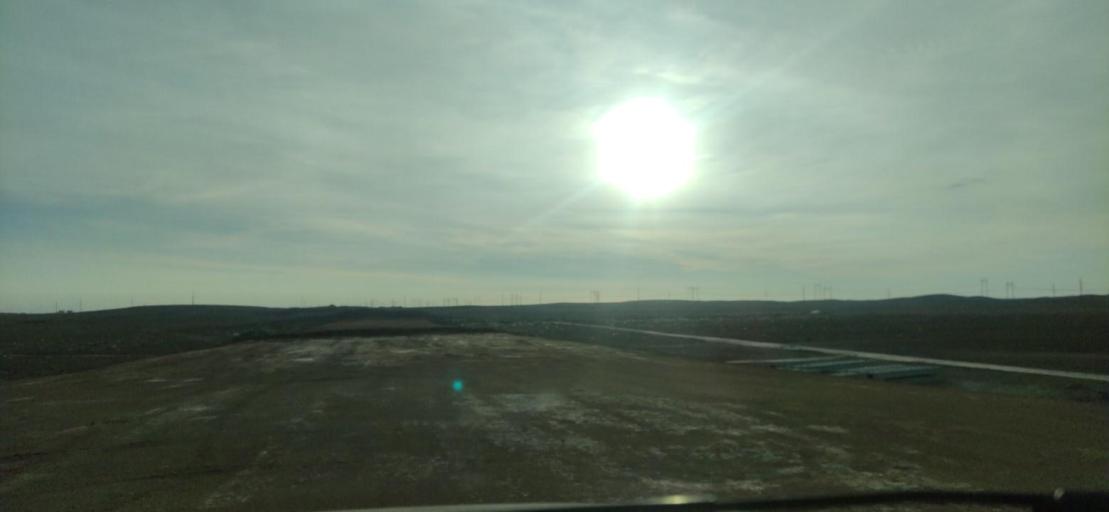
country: KZ
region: Qaraghandy
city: Saryshaghan
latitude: 46.1350
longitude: 73.6027
